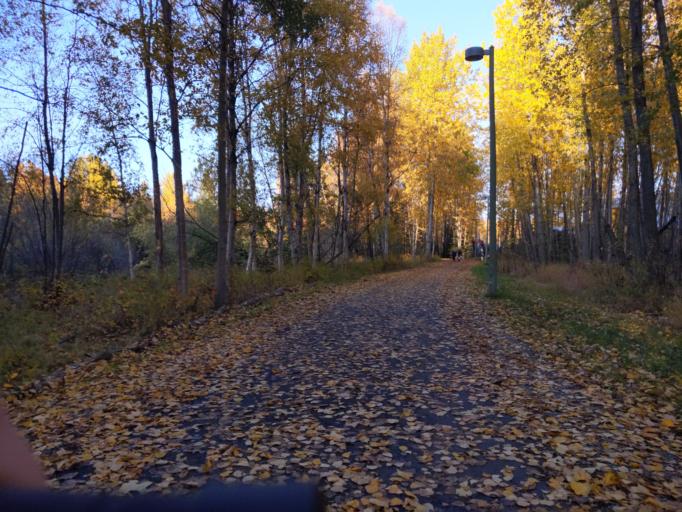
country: US
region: Alaska
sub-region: Anchorage Municipality
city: Anchorage
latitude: 61.1523
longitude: -149.8804
